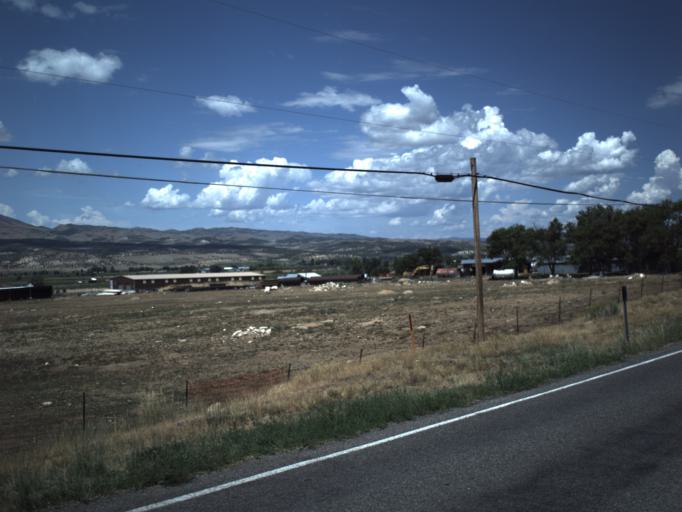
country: US
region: Utah
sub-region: Sanpete County
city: Mount Pleasant
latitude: 39.5243
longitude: -111.4706
